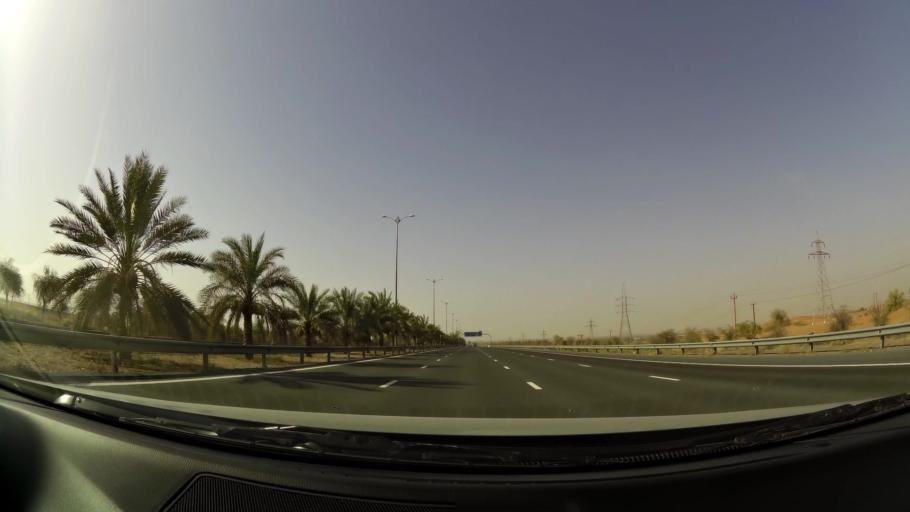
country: OM
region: Al Buraimi
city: Al Buraymi
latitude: 24.4455
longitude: 55.7844
